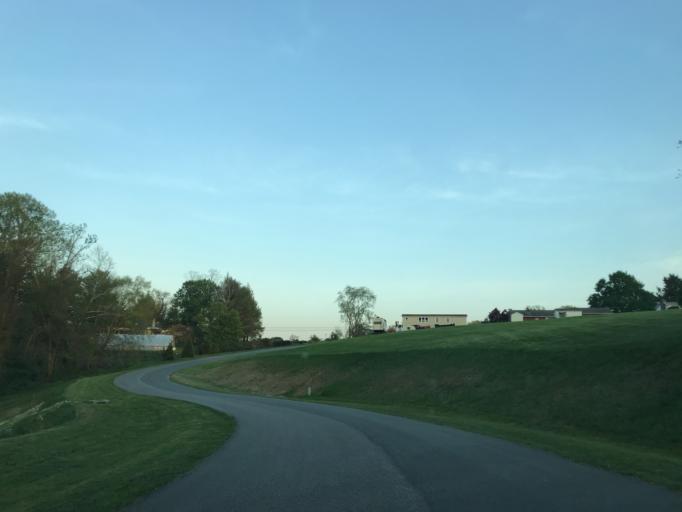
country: US
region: Maryland
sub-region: Harford County
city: Jarrettsville
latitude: 39.6008
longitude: -76.4199
